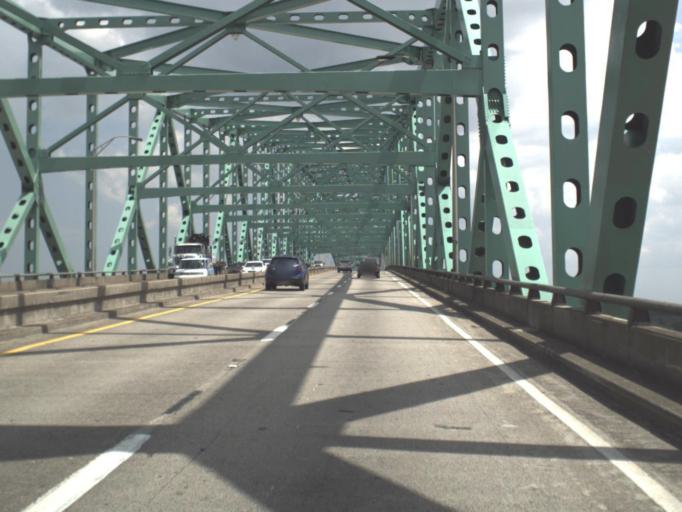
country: US
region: Florida
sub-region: Duval County
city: Jacksonville
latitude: 30.3186
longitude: -81.6297
